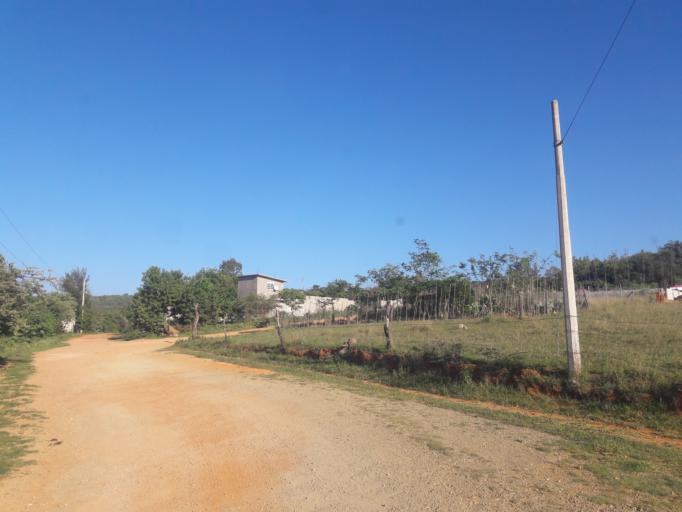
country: MX
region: Oaxaca
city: San Jeronimo Silacayoapilla
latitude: 17.8029
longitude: -97.8190
